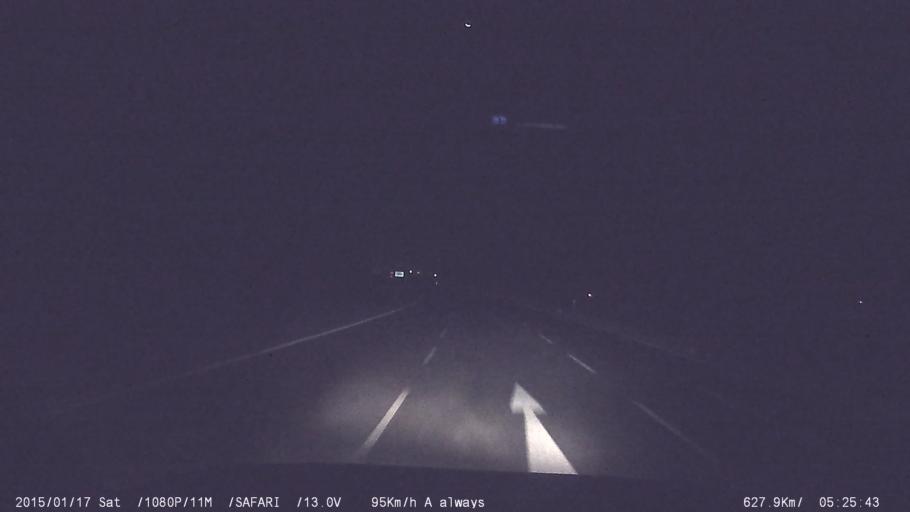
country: IN
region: Tamil Nadu
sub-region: Vellore
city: Arcot
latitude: 12.9411
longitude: 79.2368
